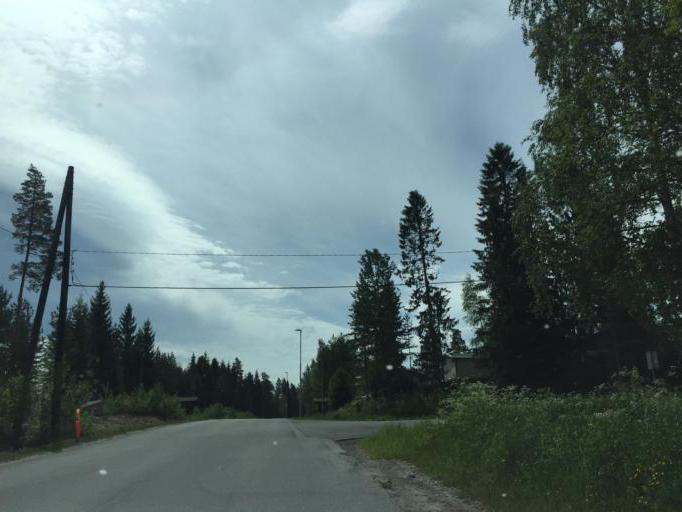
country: NO
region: Akershus
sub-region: Nes
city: Fjellfoten
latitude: 60.0909
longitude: 11.4782
